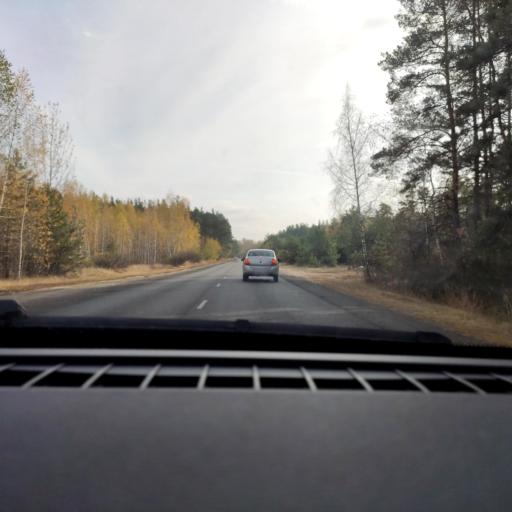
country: RU
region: Voronezj
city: Maslovka
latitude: 51.5791
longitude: 39.2891
